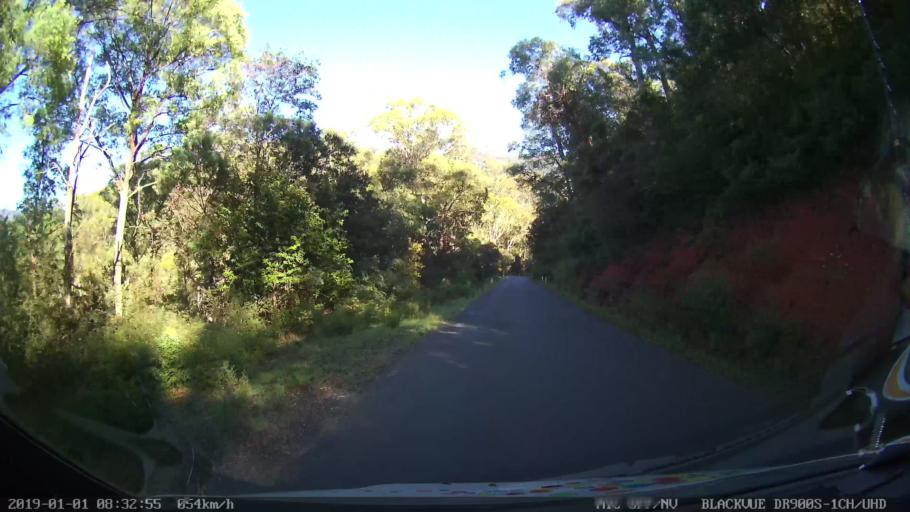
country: AU
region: New South Wales
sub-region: Snowy River
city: Jindabyne
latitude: -36.3584
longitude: 148.2046
